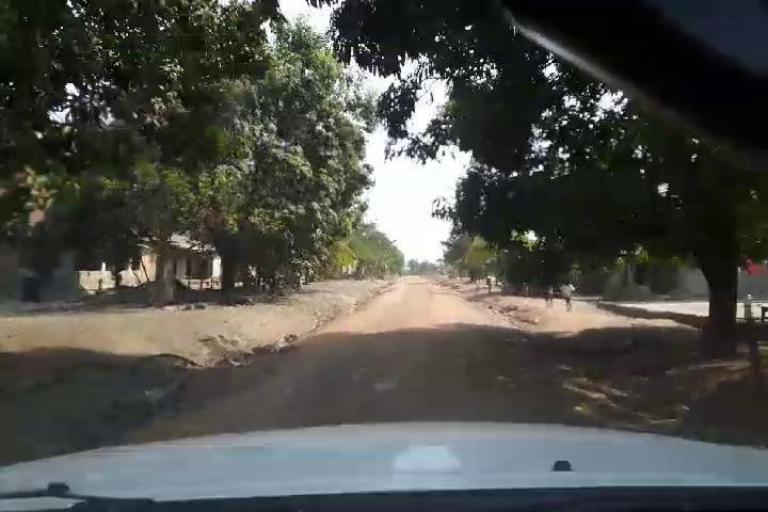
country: SL
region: Northern Province
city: Masingbi
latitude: 8.7847
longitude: -11.8720
